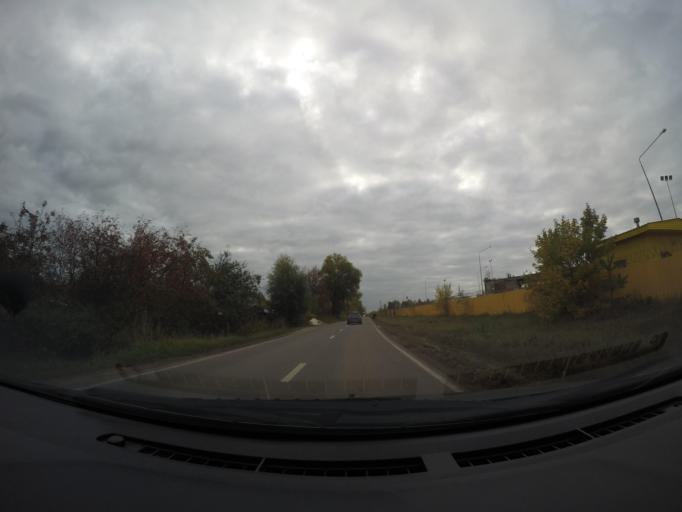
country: RU
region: Moskovskaya
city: Rechitsy
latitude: 55.6141
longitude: 38.4455
